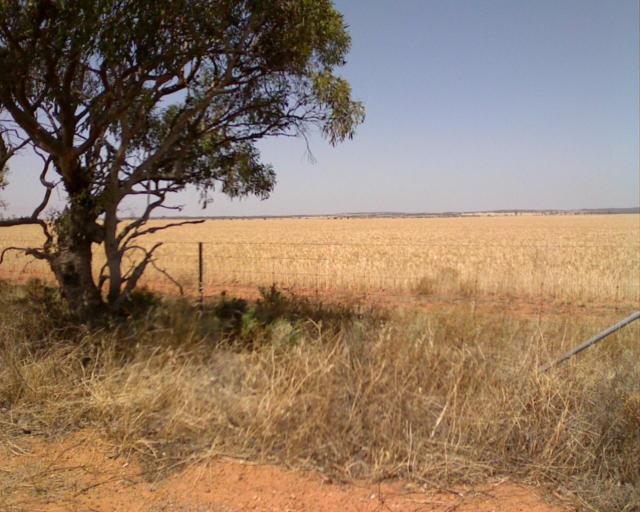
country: AU
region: Western Australia
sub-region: Merredin
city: Merredin
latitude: -30.8322
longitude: 118.2093
